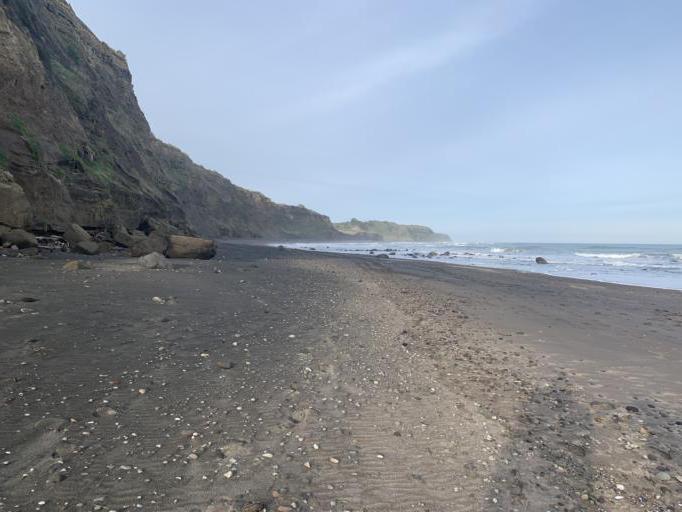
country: NZ
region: Taranaki
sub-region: South Taranaki District
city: Opunake
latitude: -39.5627
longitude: 174.0499
